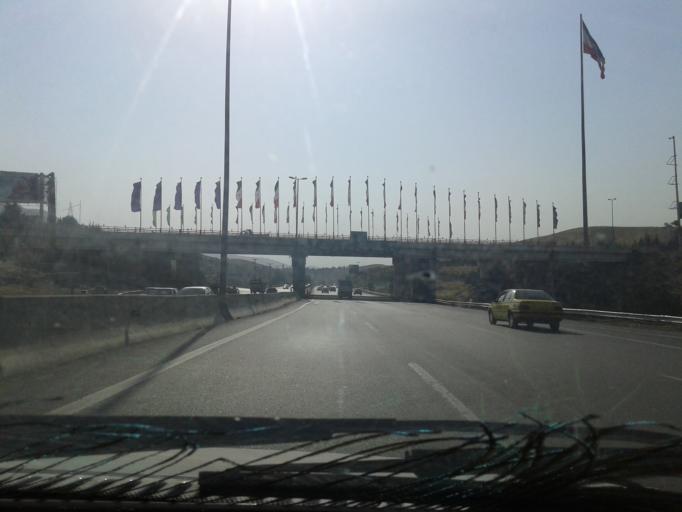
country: IR
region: Tehran
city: Tehran
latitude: 35.7308
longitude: 51.6363
